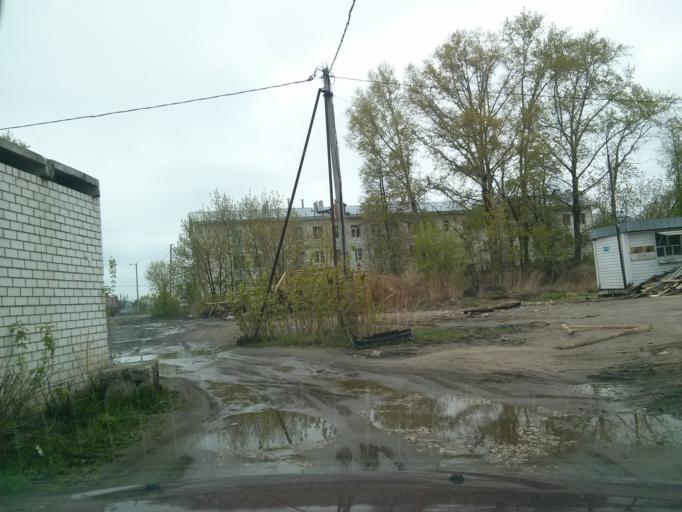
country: RU
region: Vladimir
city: Murom
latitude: 55.5659
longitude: 42.0724
